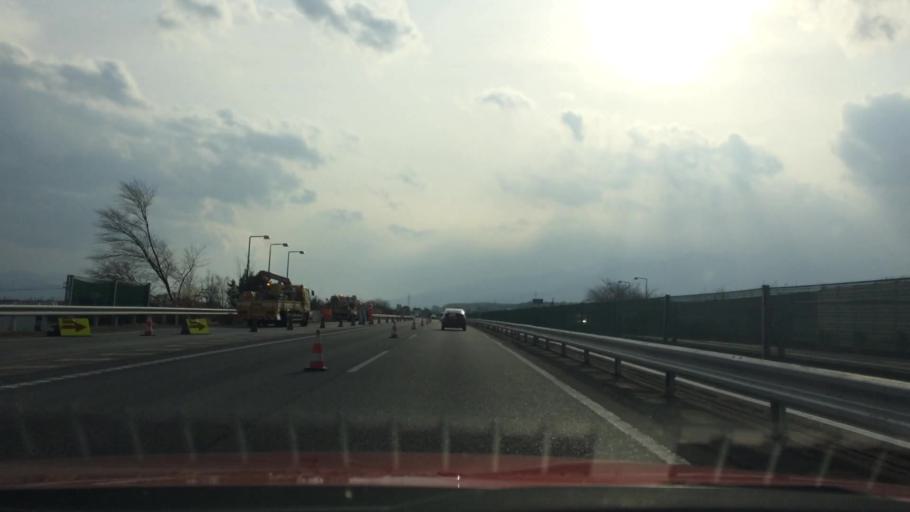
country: JP
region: Nagano
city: Tatsuno
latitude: 35.9137
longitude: 137.9665
